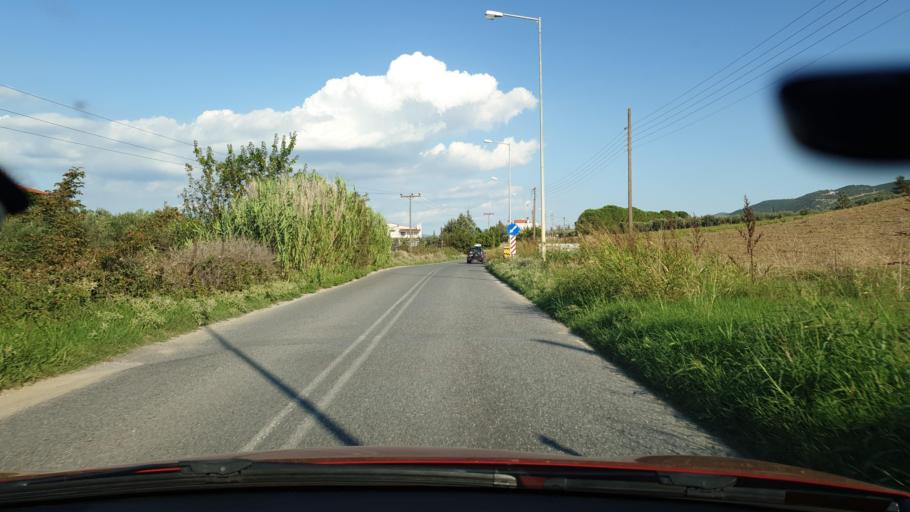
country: GR
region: Central Macedonia
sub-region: Nomos Thessalonikis
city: Agia Paraskevi
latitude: 40.4889
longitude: 23.0367
